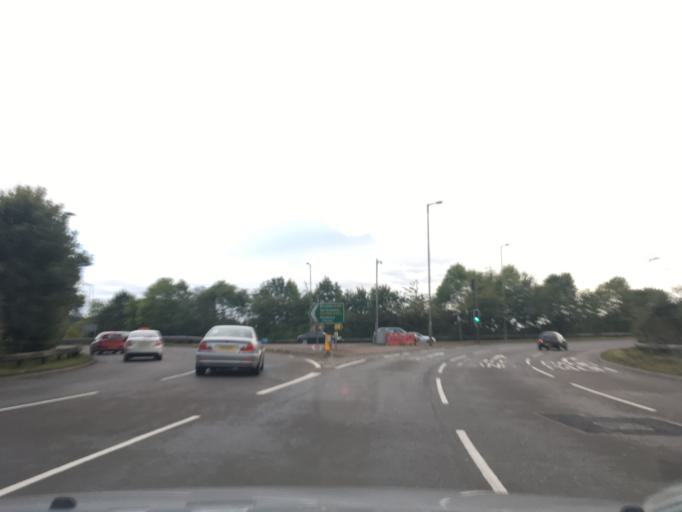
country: GB
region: England
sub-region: Oxfordshire
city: Banbury
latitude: 52.0733
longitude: -1.3118
